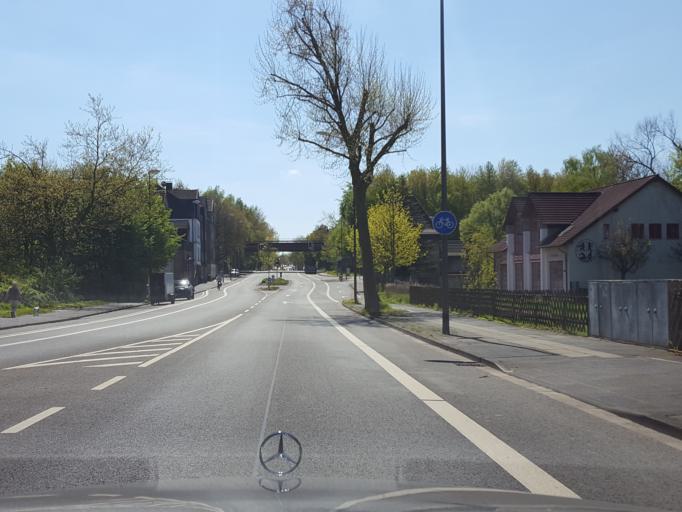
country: DE
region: North Rhine-Westphalia
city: Castrop-Rauxel
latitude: 51.5332
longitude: 7.3200
